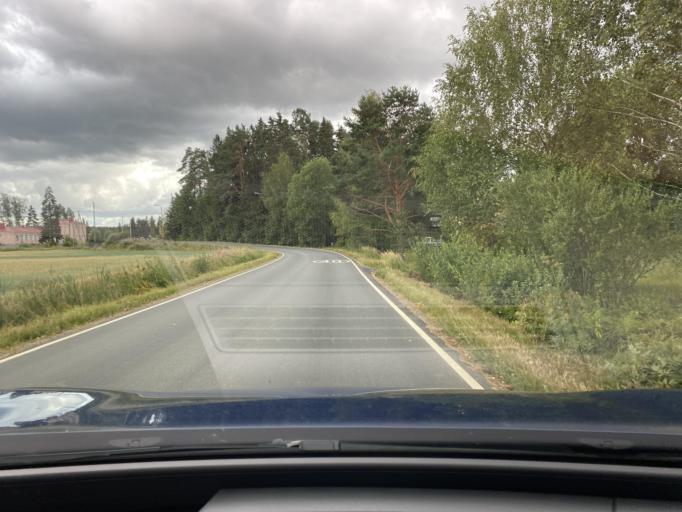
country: FI
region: Pirkanmaa
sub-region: Lounais-Pirkanmaa
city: Punkalaidun
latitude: 61.2349
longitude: 23.1246
